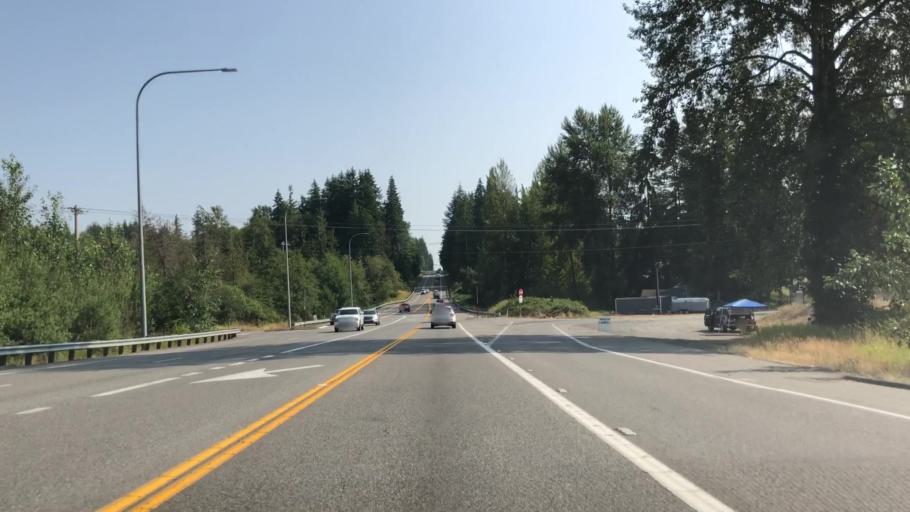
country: US
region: Washington
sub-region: Snohomish County
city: West Lake Stevens
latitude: 47.9754
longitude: -122.1027
